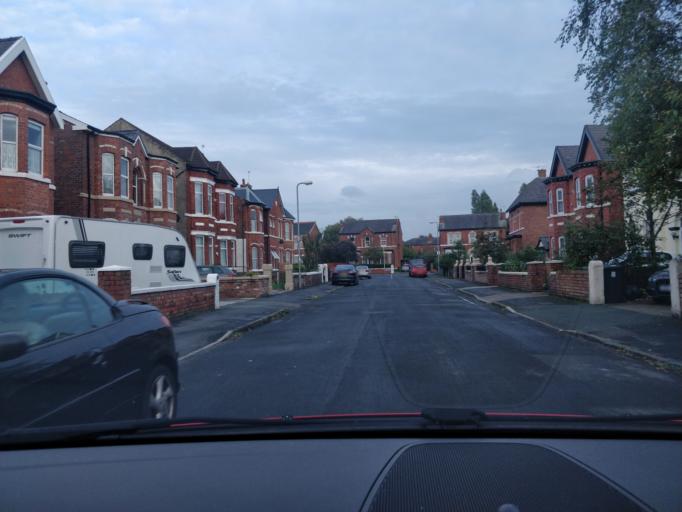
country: GB
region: England
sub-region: Sefton
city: Southport
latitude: 53.6417
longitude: -2.9949
